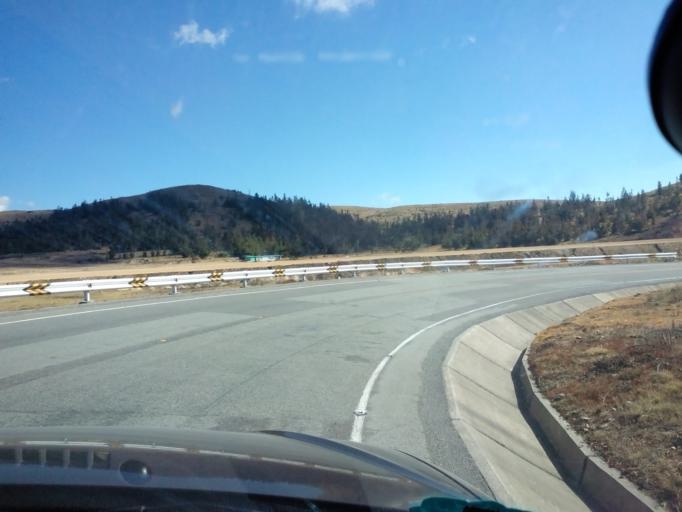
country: PE
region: Apurimac
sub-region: Provincia de Abancay
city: Cachora
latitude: -13.5691
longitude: -72.8225
